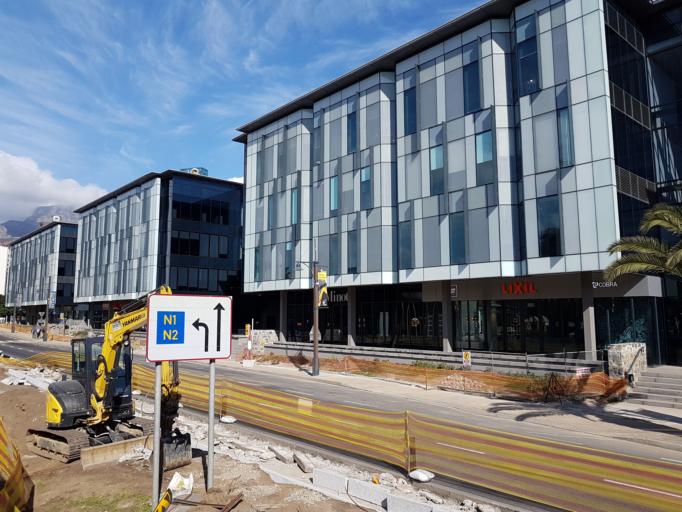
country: ZA
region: Western Cape
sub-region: City of Cape Town
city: Cape Town
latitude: -33.9122
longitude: 18.4229
